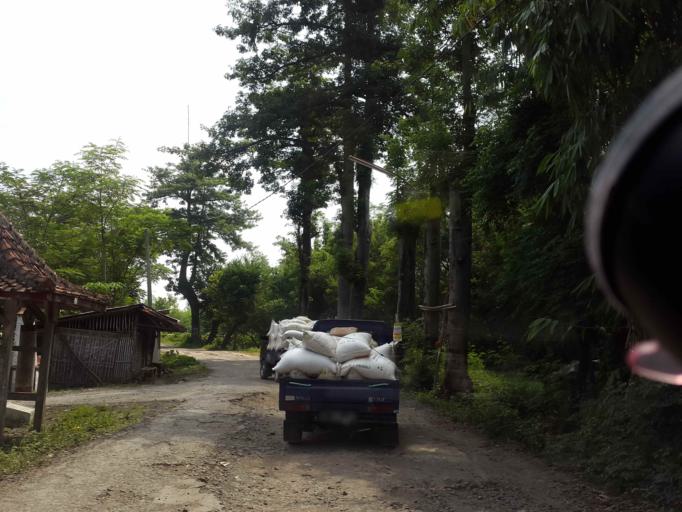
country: ID
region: Central Java
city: Pemalang
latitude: -6.9475
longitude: 109.3488
